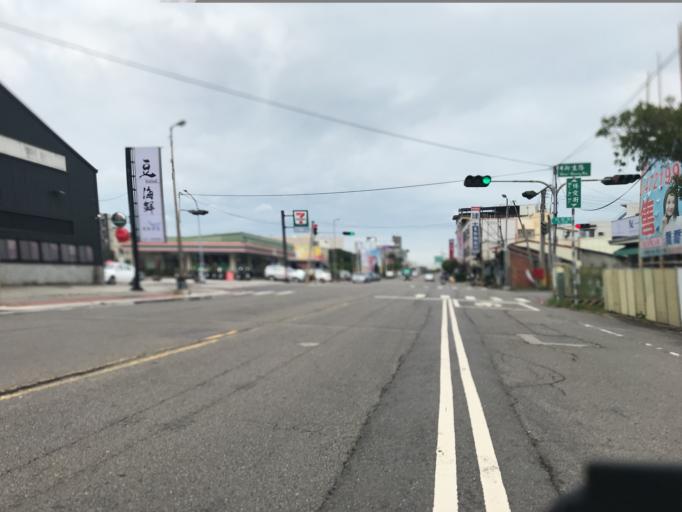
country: TW
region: Taiwan
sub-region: Miaoli
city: Miaoli
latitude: 24.6885
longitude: 120.8683
